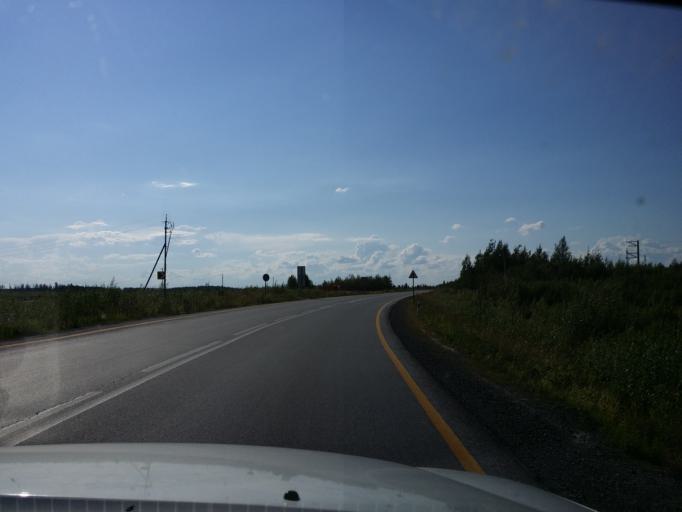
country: RU
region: Khanty-Mansiyskiy Avtonomnyy Okrug
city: Lokosovo
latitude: 61.3938
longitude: 74.8758
